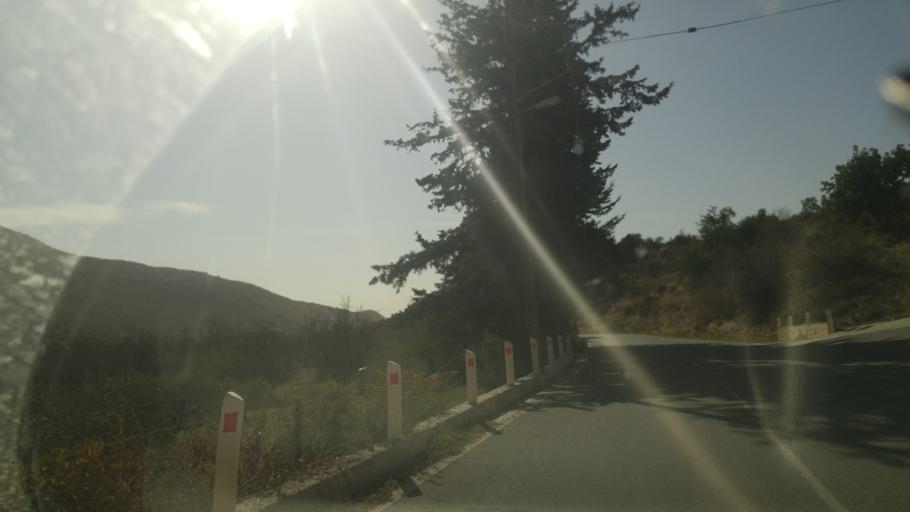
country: CY
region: Limassol
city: Pano Polemidia
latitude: 34.7549
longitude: 33.0307
